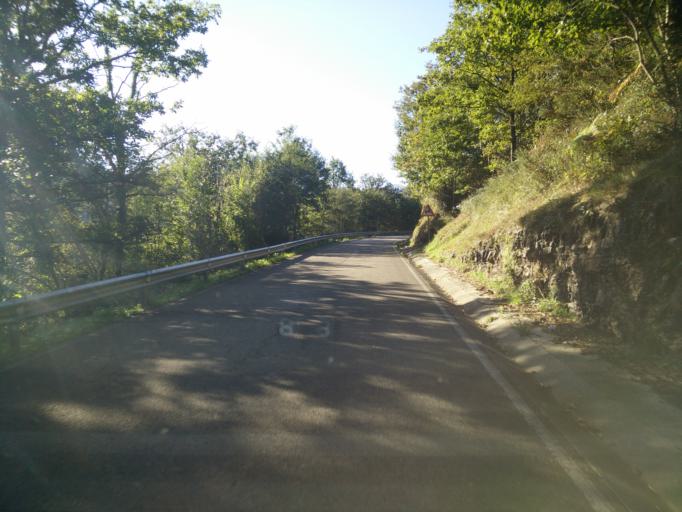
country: ES
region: Cantabria
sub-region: Provincia de Cantabria
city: San Pedro del Romeral
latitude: 43.1361
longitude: -3.8148
